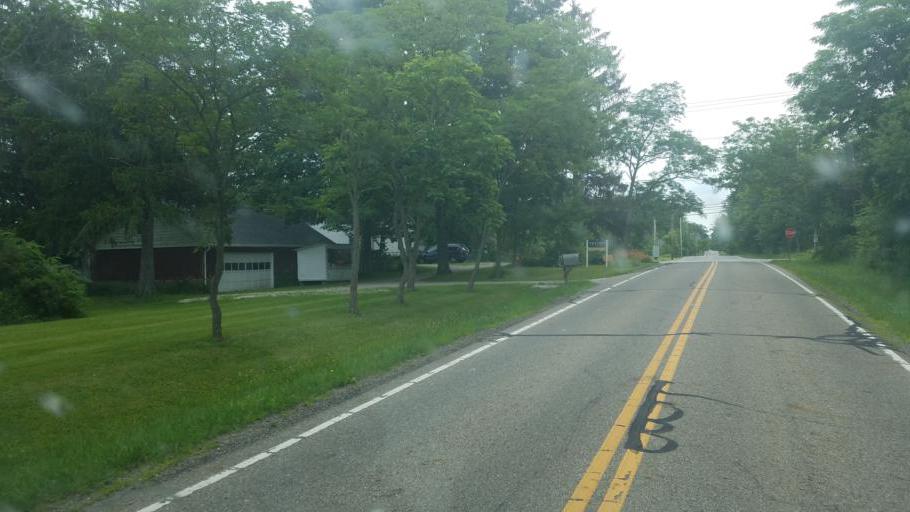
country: US
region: Ohio
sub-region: Geauga County
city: Burton
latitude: 41.4971
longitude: -81.1461
